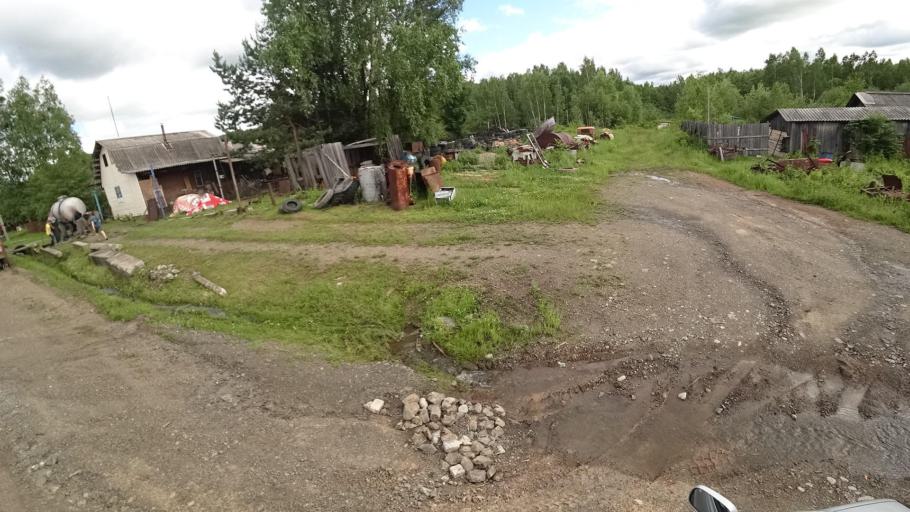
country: RU
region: Khabarovsk Krai
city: Litovko
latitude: 49.3637
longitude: 135.1678
